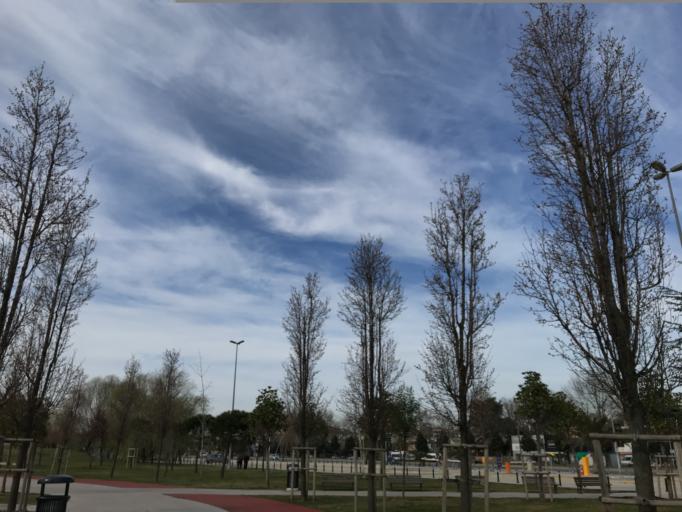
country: TR
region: Istanbul
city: Maltepe
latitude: 40.9367
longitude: 29.1129
